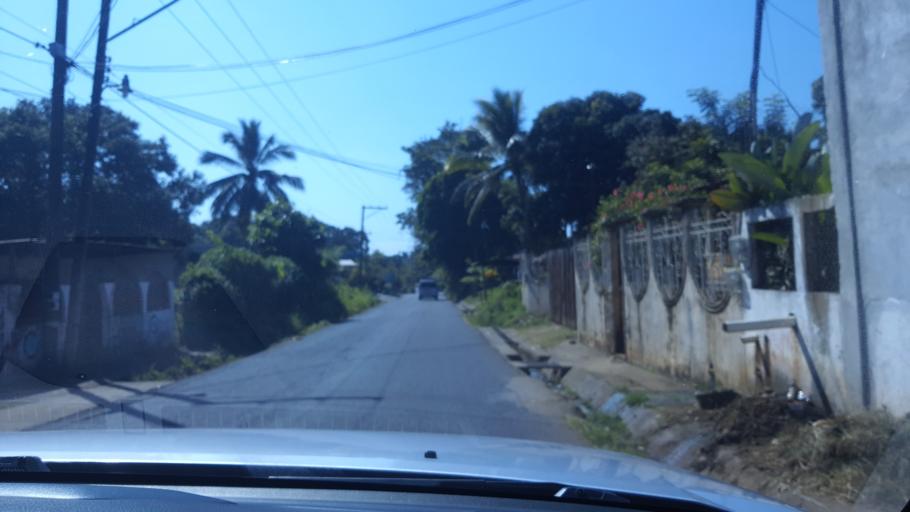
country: GT
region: Quetzaltenango
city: Flores Costa Cuca
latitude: 14.6355
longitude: -91.9266
